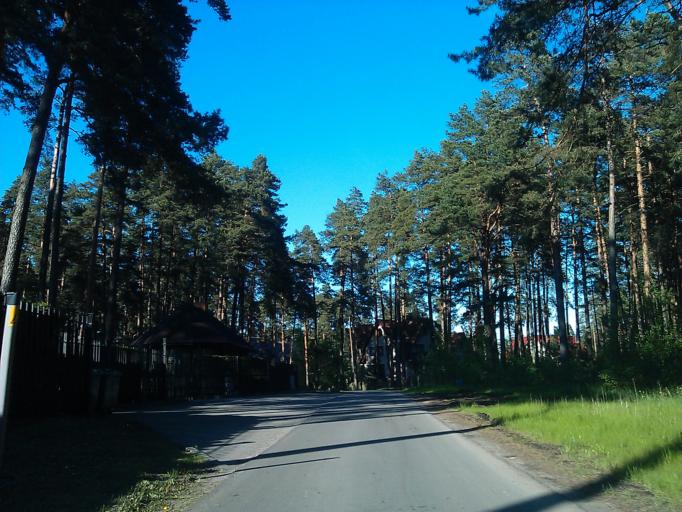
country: LV
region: Riga
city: Bergi
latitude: 57.0137
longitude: 24.2845
